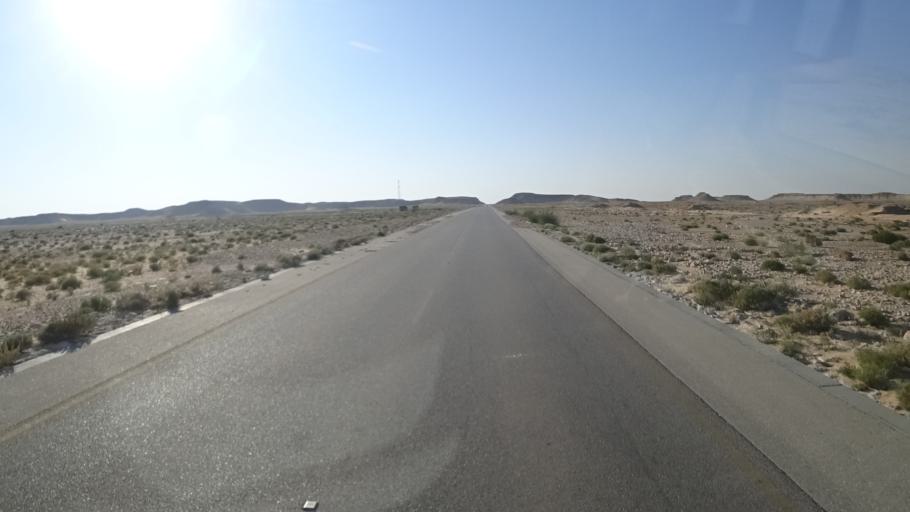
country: OM
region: Zufar
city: Salalah
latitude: 17.6404
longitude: 53.8655
